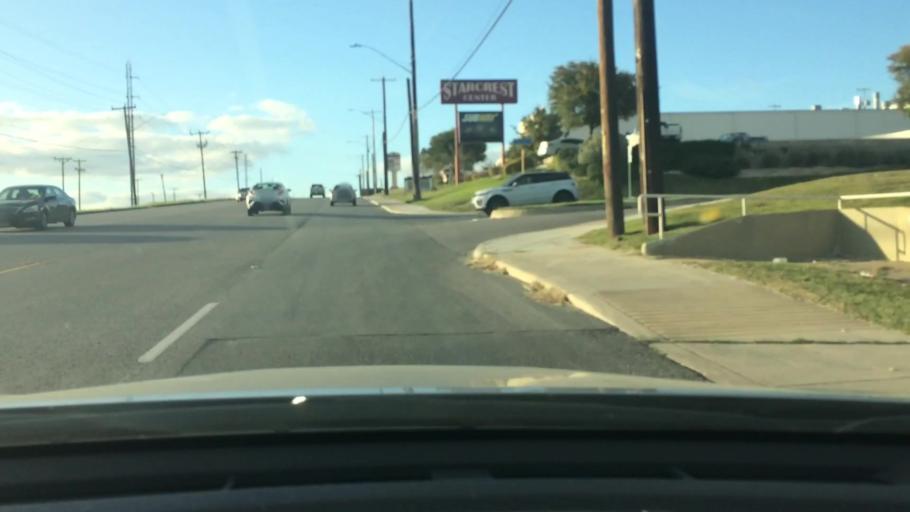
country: US
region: Texas
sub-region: Bexar County
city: Hollywood Park
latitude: 29.5505
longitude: -98.4649
